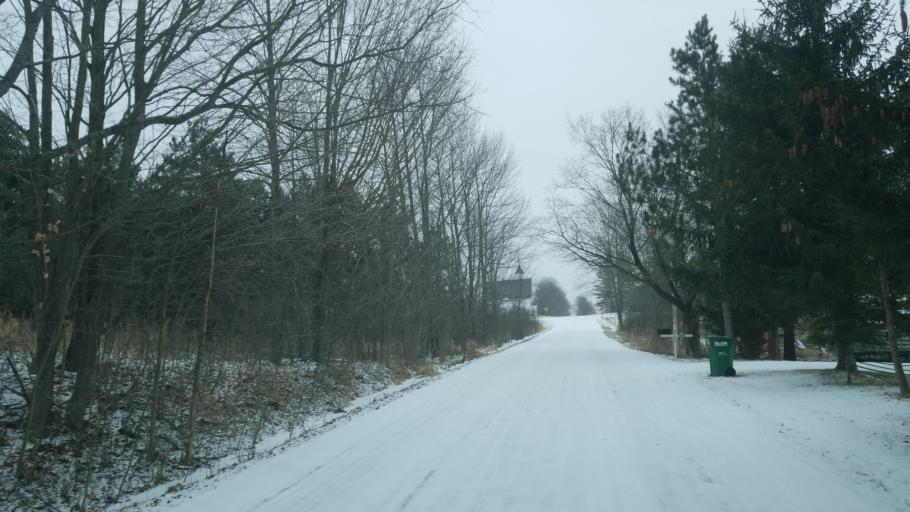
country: US
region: Michigan
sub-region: Osceola County
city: Evart
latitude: 44.0159
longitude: -85.2286
